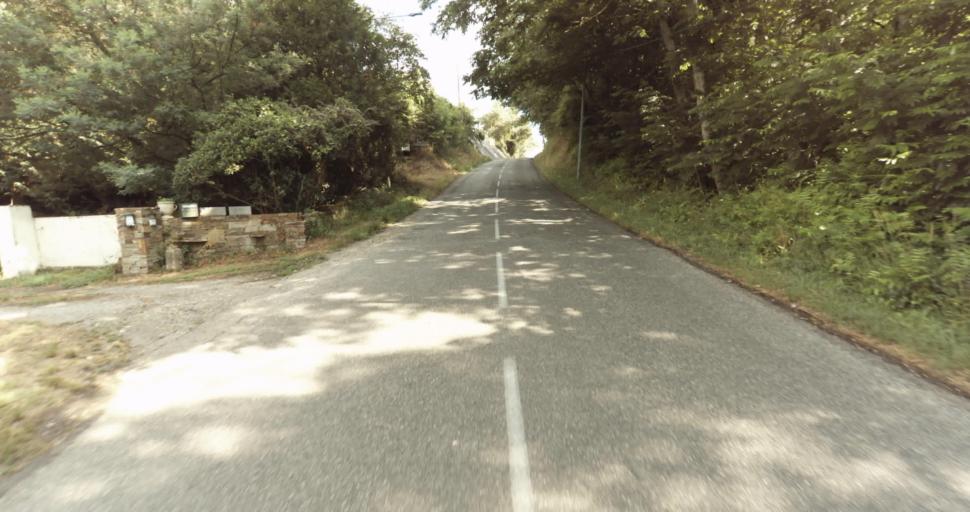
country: FR
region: Midi-Pyrenees
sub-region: Departement de la Haute-Garonne
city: Fonsorbes
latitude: 43.5660
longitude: 1.2336
